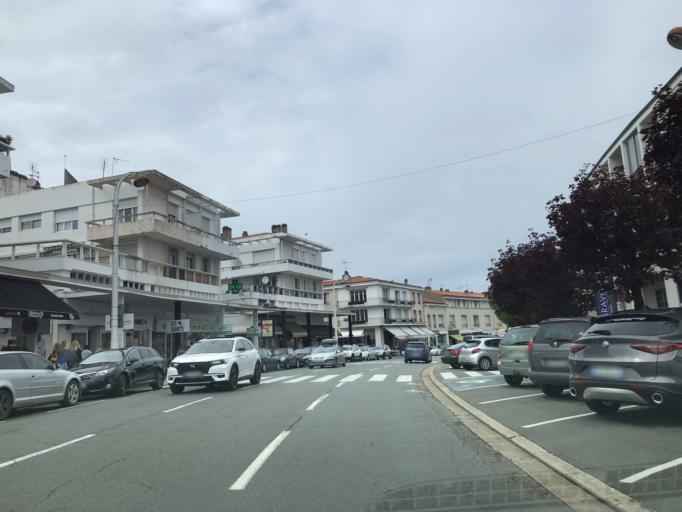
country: FR
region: Poitou-Charentes
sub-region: Departement de la Charente-Maritime
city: Royan
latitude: 45.6218
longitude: -1.0312
